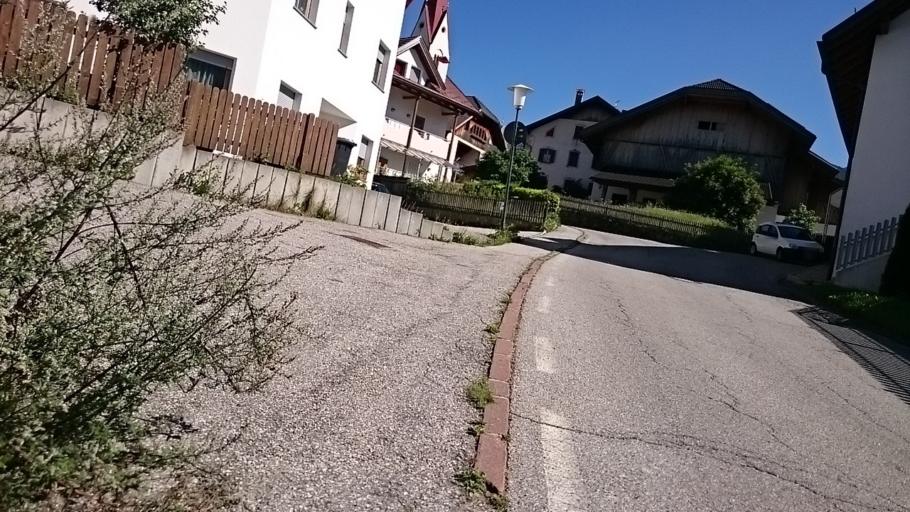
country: IT
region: Trentino-Alto Adige
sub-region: Bolzano
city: Valdaora di Mezzo
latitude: 46.7689
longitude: 12.0158
